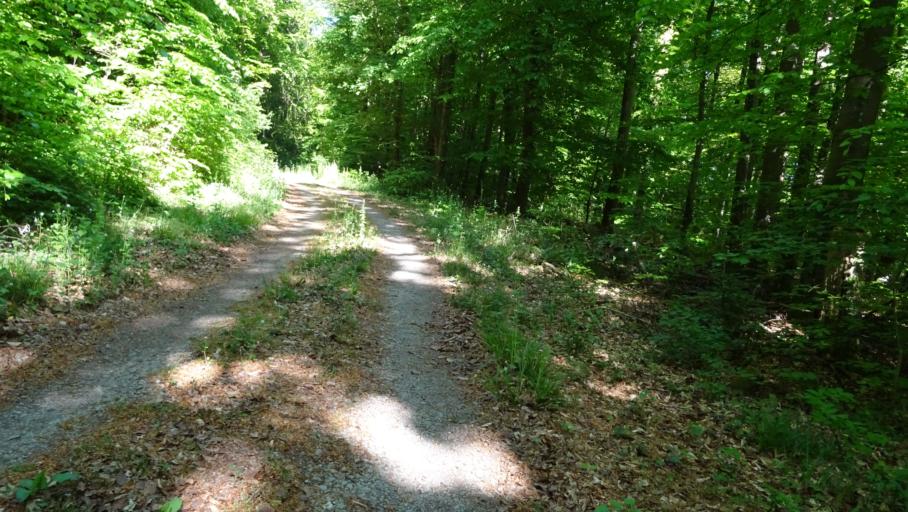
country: DE
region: Baden-Wuerttemberg
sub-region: Karlsruhe Region
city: Neckarzimmern
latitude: 49.3250
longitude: 9.1277
